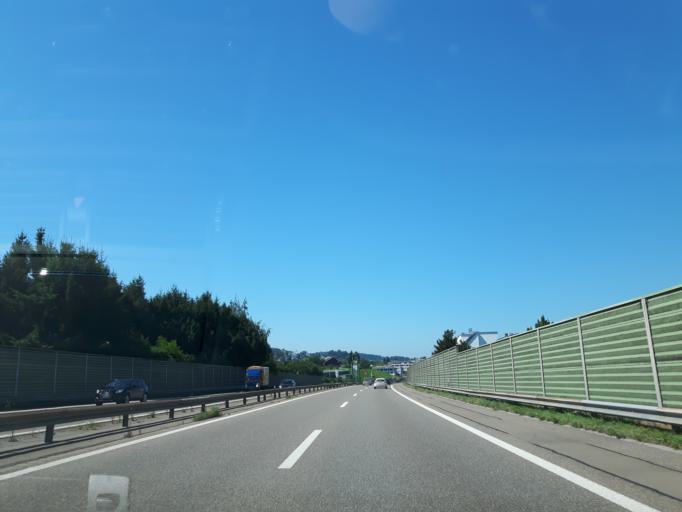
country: CH
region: Schwyz
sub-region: Bezirk March
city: Lachen
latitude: 47.1862
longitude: 8.8481
